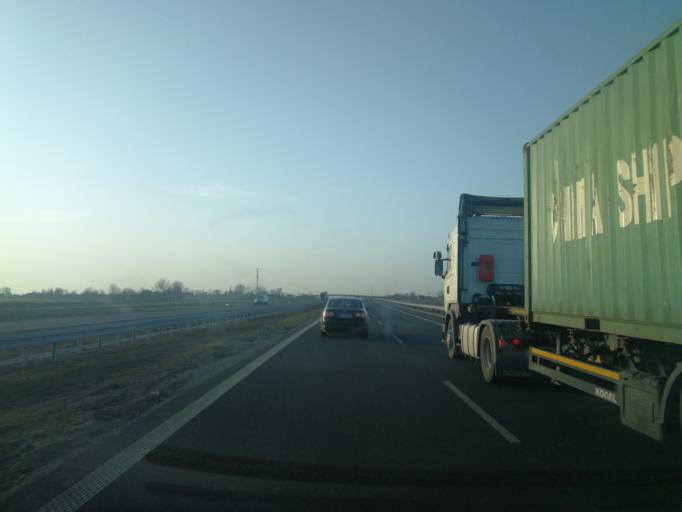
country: PL
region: Pomeranian Voivodeship
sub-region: Powiat nowodworski
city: Ostaszewo
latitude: 54.2459
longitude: 18.9957
